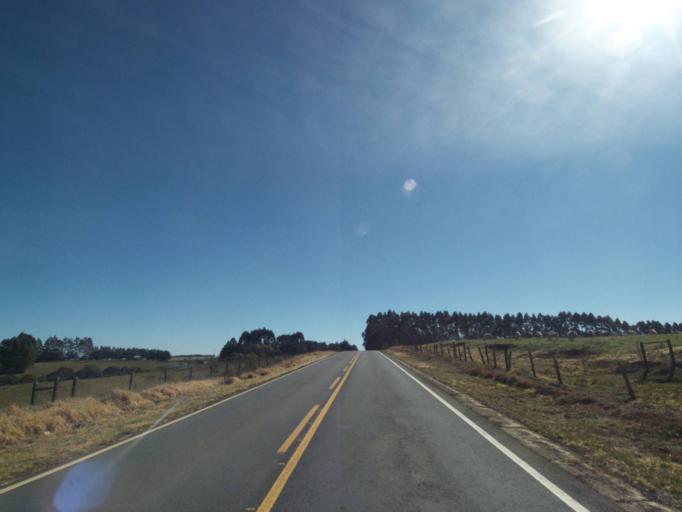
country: BR
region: Parana
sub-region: Castro
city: Castro
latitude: -24.7183
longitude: -50.1889
